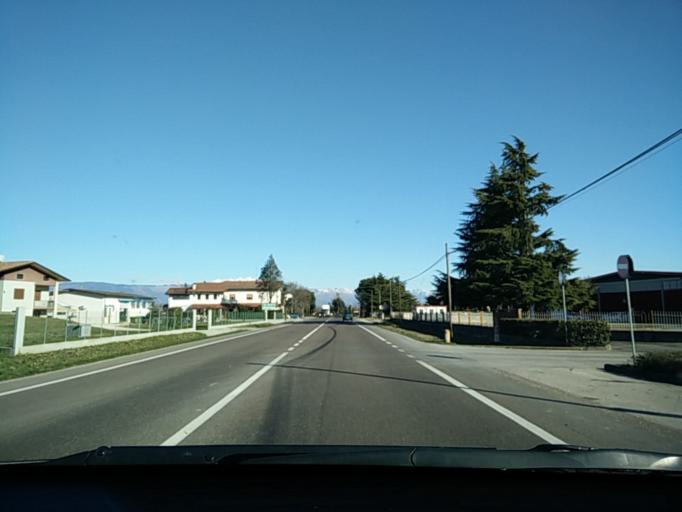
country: IT
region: Veneto
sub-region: Provincia di Treviso
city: Mansue
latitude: 45.8352
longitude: 12.5372
